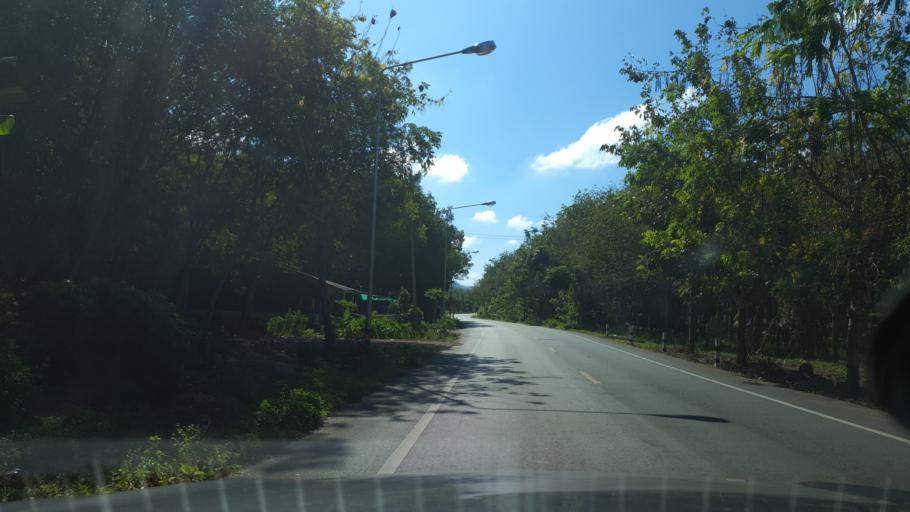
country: TH
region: Phangnga
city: Ban Ao Nang
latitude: 8.0753
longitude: 98.8056
